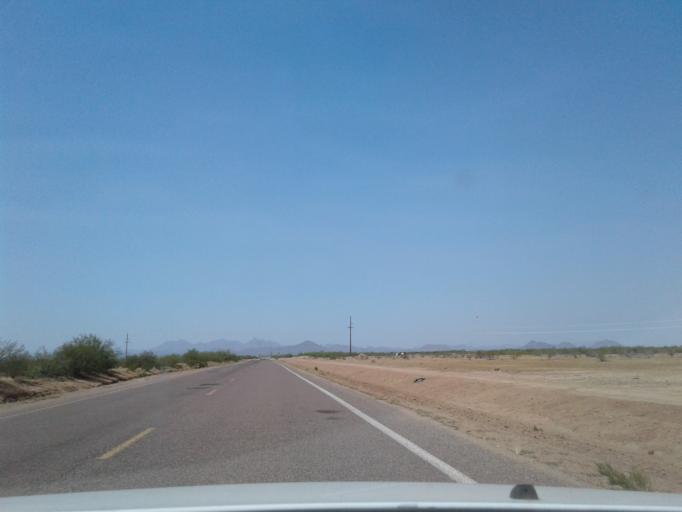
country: US
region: Arizona
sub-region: Pima County
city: Avra Valley
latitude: 32.6041
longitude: -111.3239
